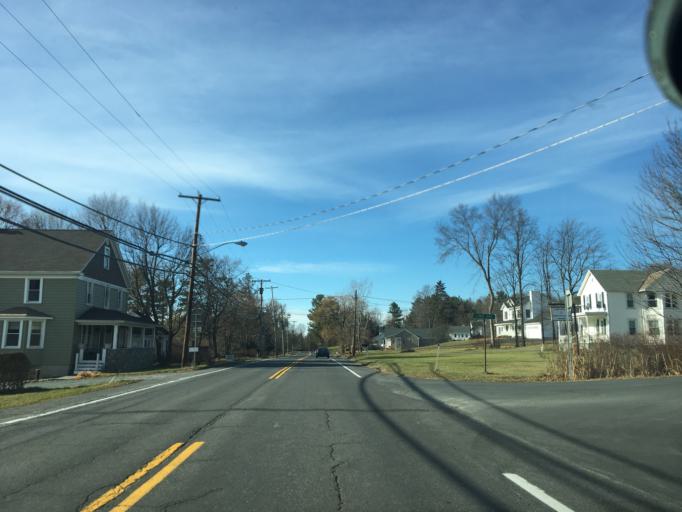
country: US
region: New York
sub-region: Rensselaer County
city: Averill Park
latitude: 42.6355
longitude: -73.5595
